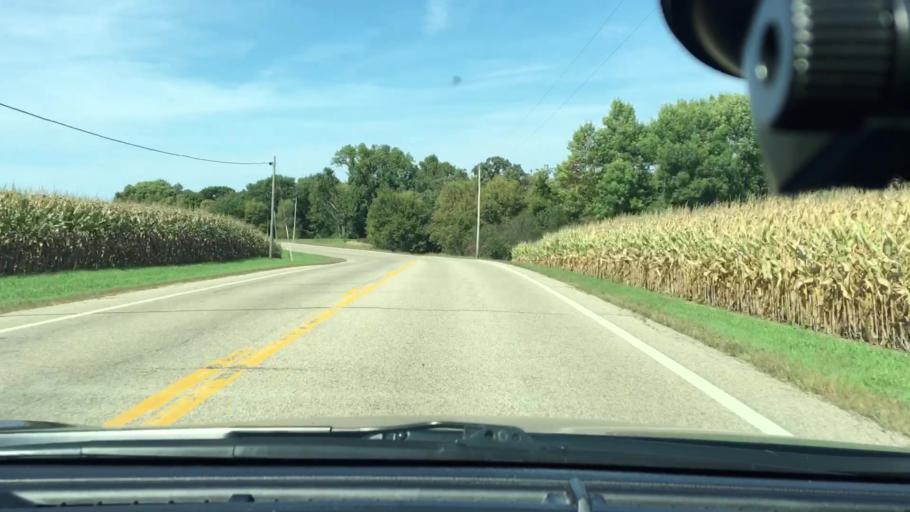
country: US
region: Minnesota
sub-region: Hennepin County
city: Corcoran
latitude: 45.1111
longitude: -93.5684
